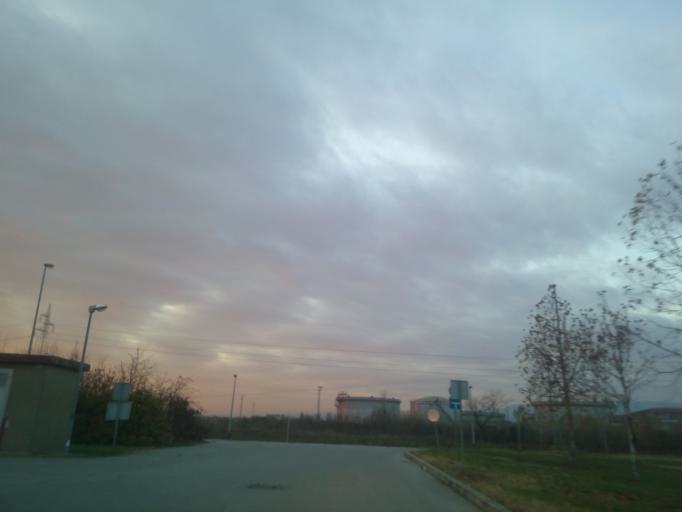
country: HR
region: Zagrebacka
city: Micevec
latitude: 45.7876
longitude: 16.0795
